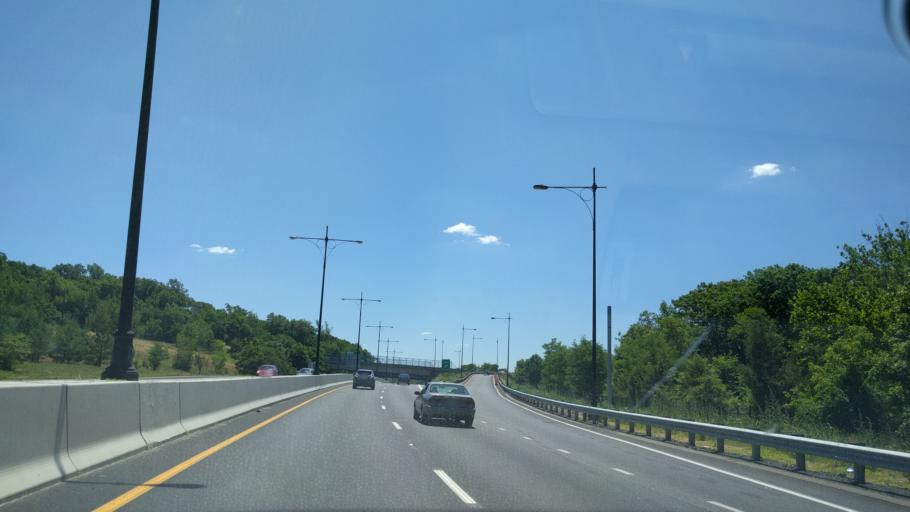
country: US
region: Massachusetts
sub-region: Worcester County
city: Millbury
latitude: 42.2137
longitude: -71.7832
